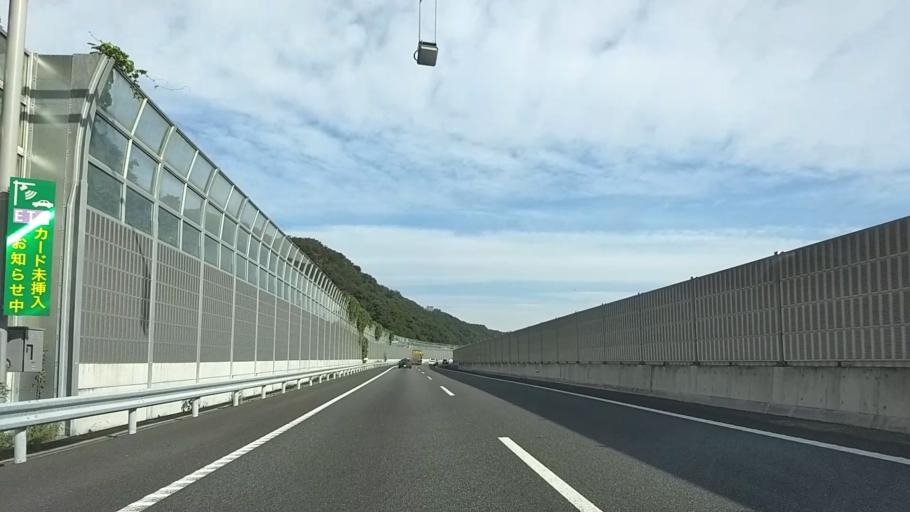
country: JP
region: Kanagawa
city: Zama
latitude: 35.4978
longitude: 139.3664
